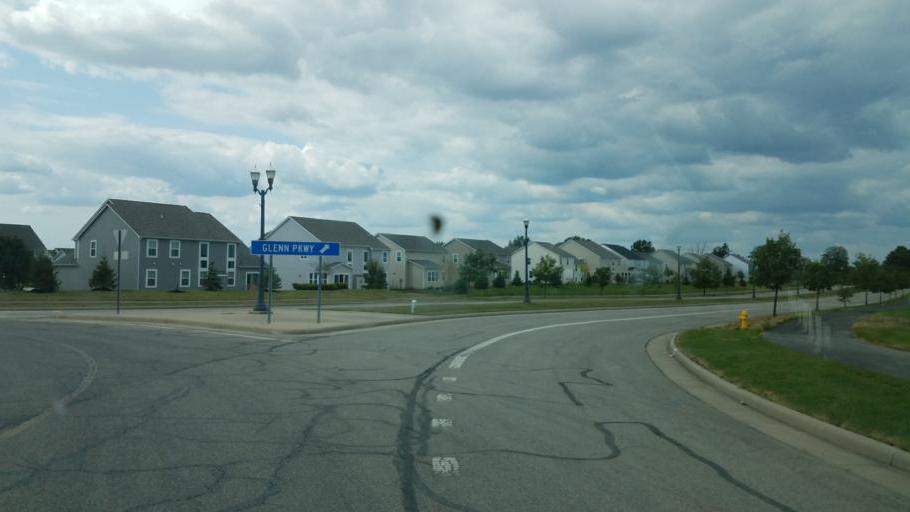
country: US
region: Ohio
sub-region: Delaware County
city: Lewis Center
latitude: 40.2485
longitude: -83.0340
